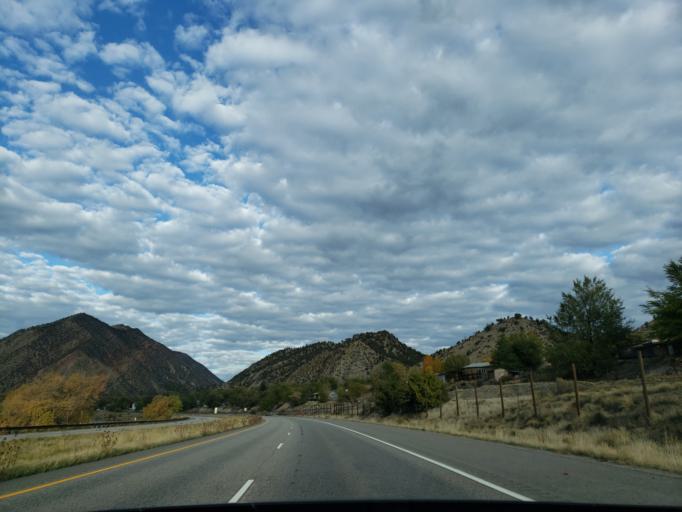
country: US
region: Colorado
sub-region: Garfield County
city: New Castle
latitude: 39.5687
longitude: -107.5228
